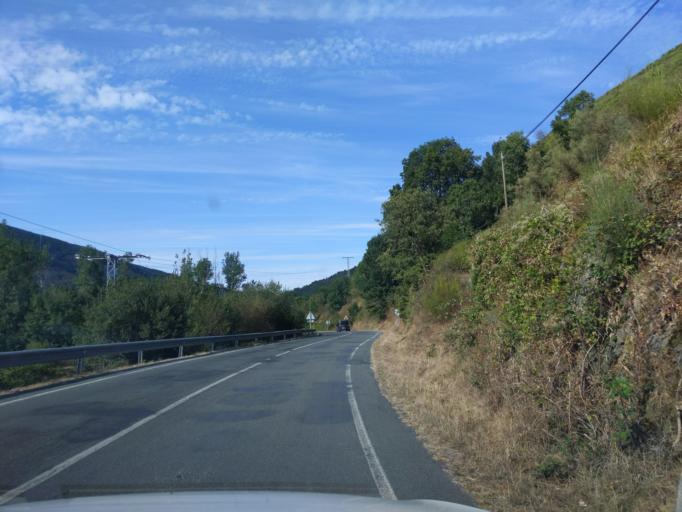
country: ES
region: La Rioja
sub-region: Provincia de La Rioja
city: Zorraquin
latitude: 42.2831
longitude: -3.0269
